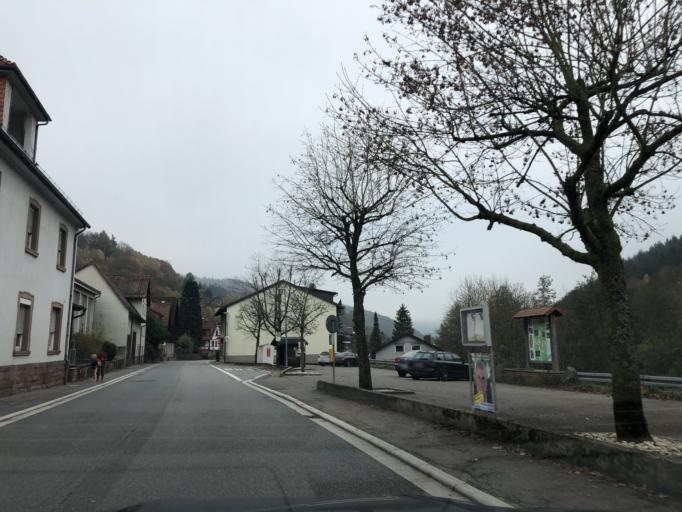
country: DE
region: Baden-Wuerttemberg
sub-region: Karlsruhe Region
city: Heiligkreuzsteinach
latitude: 49.4613
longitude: 8.8060
